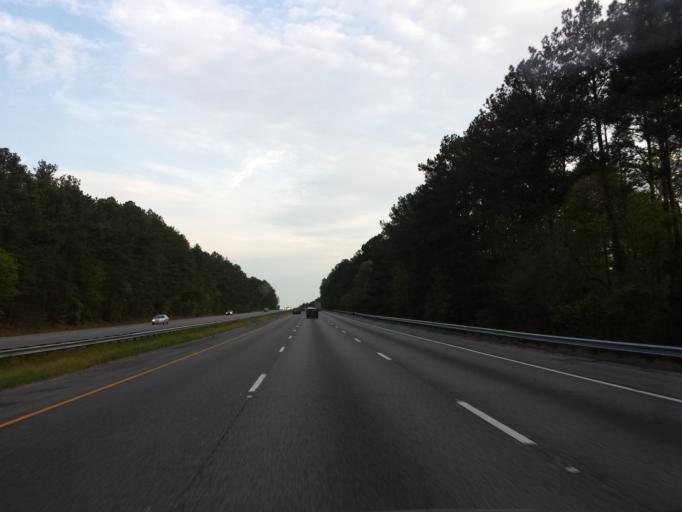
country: US
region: Georgia
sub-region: Houston County
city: Perry
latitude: 32.3927
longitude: -83.7667
